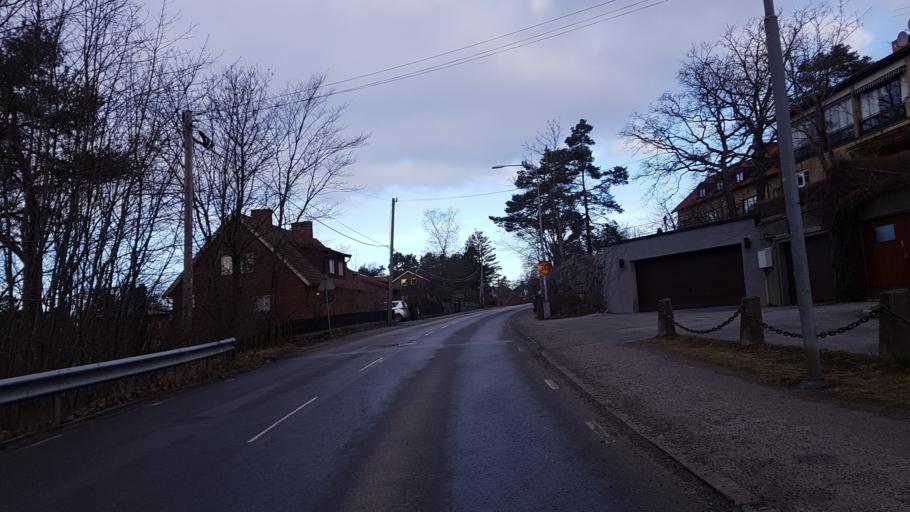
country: SE
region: Stockholm
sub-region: Lidingo
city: Lidingoe
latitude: 59.3577
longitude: 18.1282
